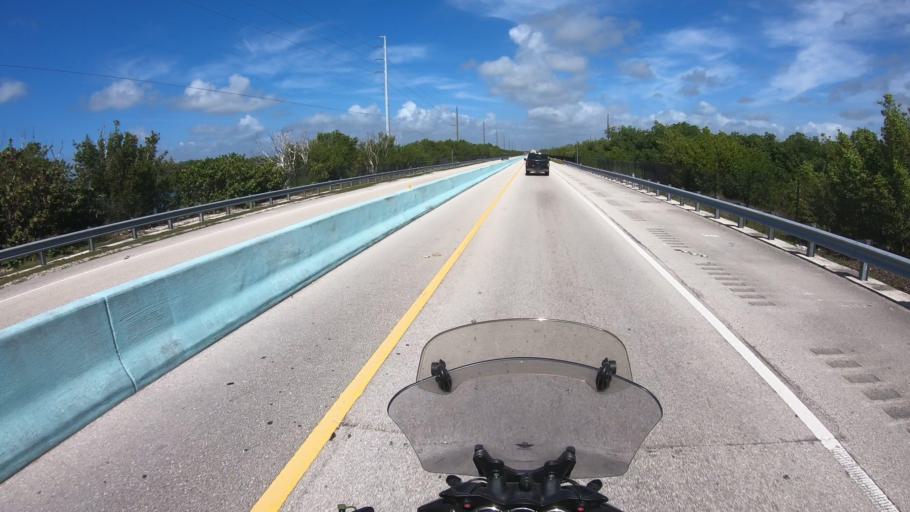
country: US
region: Florida
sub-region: Monroe County
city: North Key Largo
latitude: 25.2162
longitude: -80.4266
